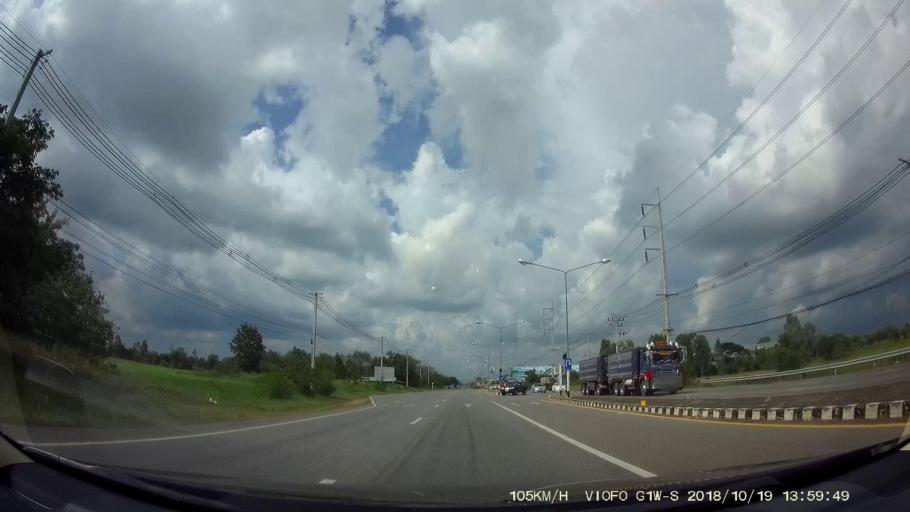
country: TH
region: Chaiyaphum
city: Chaiyaphum
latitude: 15.8154
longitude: 102.0602
